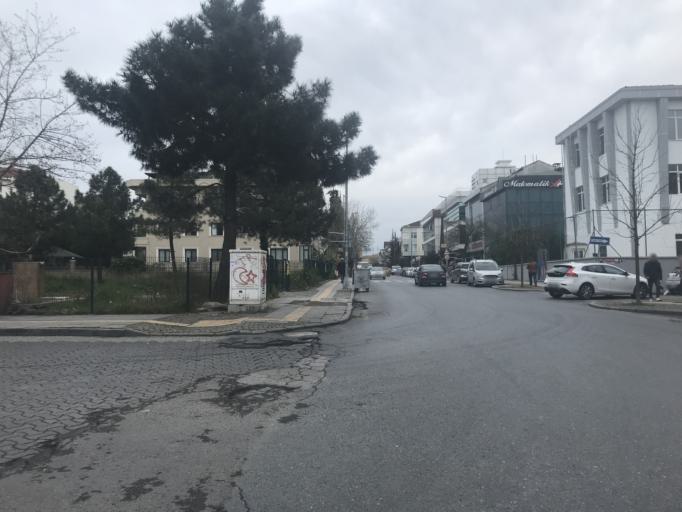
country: TR
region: Istanbul
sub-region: Atasehir
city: Atasehir
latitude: 40.9866
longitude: 29.1329
